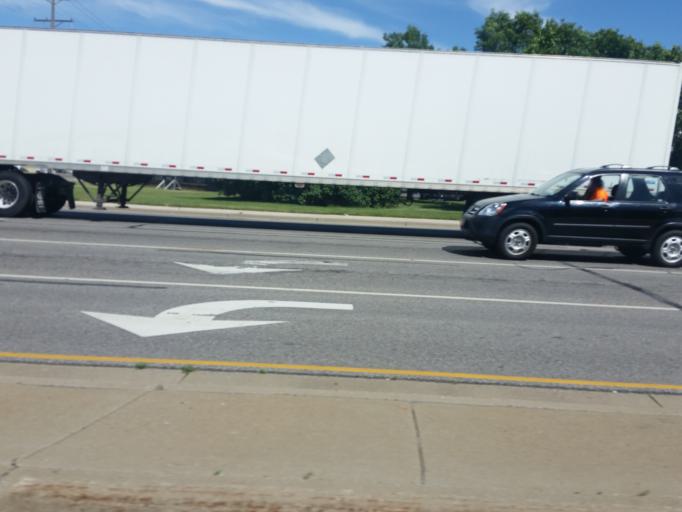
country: US
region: Minnesota
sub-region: Stearns County
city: Waite Park
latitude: 45.5529
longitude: -94.2052
